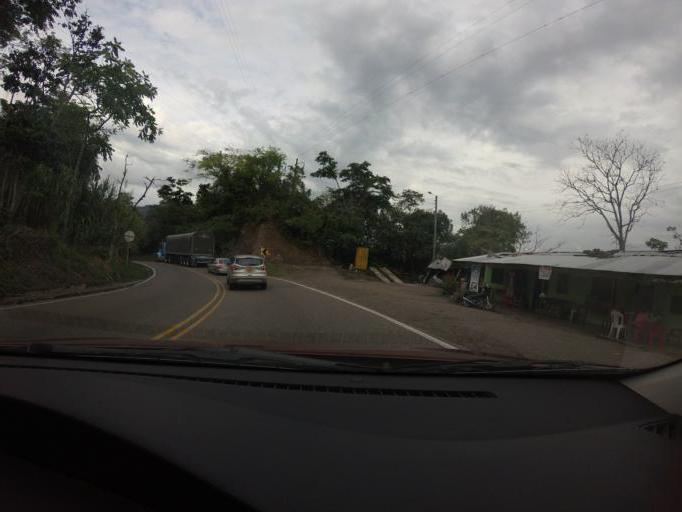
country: CO
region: Cundinamarca
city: Villeta
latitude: 5.0277
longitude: -74.5080
